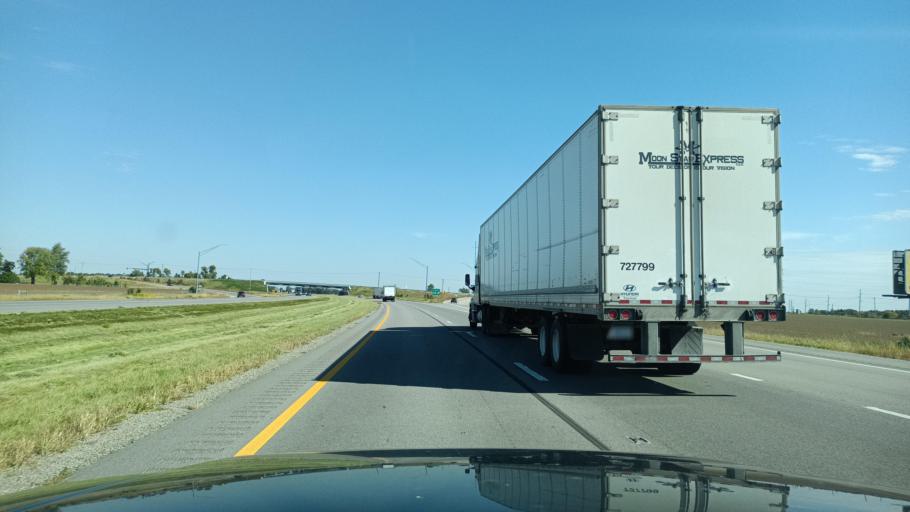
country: US
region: Ohio
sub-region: Defiance County
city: Defiance
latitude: 41.3093
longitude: -84.3289
